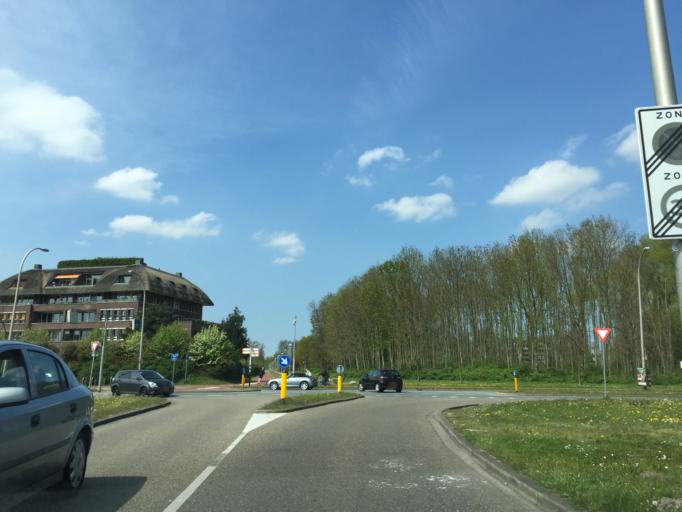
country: NL
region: South Holland
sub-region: Gemeente Den Haag
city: Ypenburg
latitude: 52.0467
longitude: 4.3721
